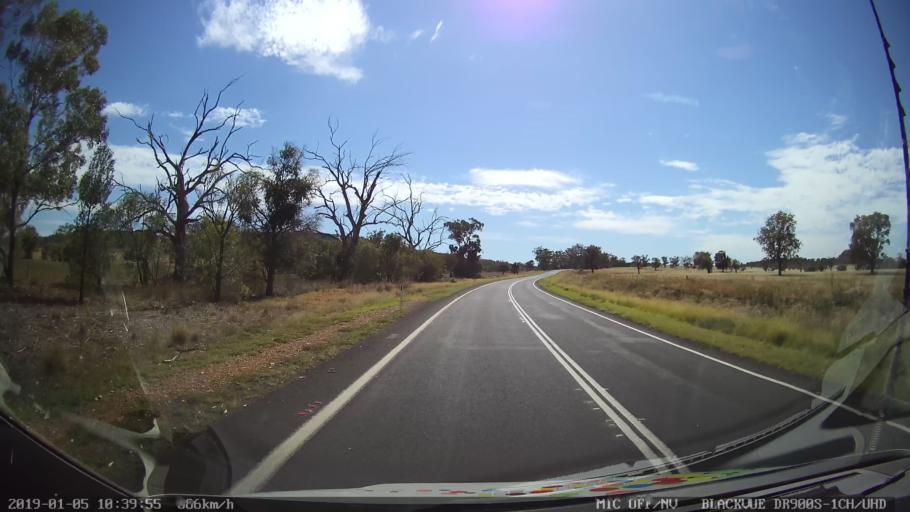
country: AU
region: New South Wales
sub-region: Gilgandra
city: Gilgandra
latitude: -31.4658
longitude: 148.9369
